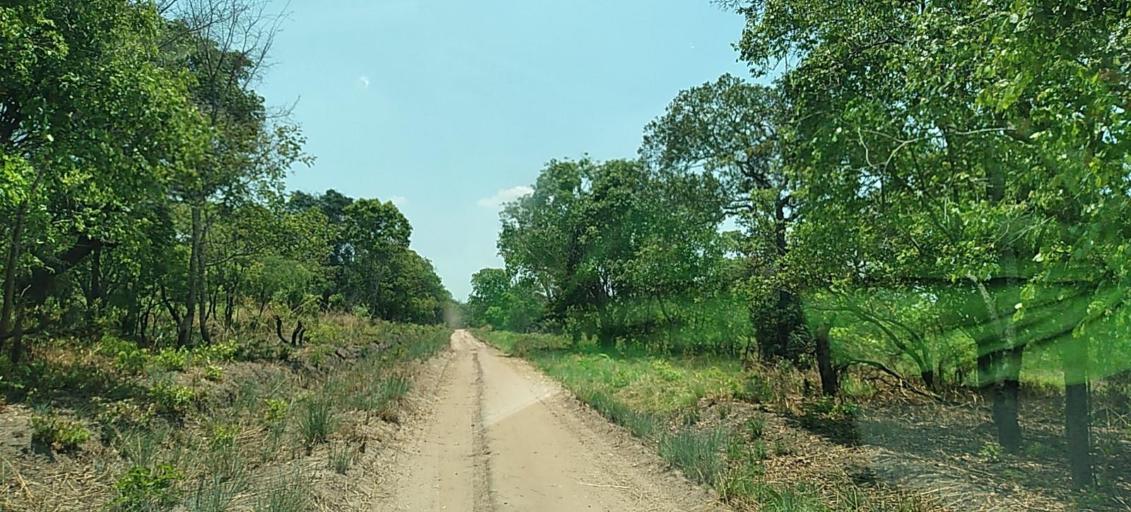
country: CD
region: Katanga
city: Kolwezi
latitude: -11.3672
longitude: 25.2096
